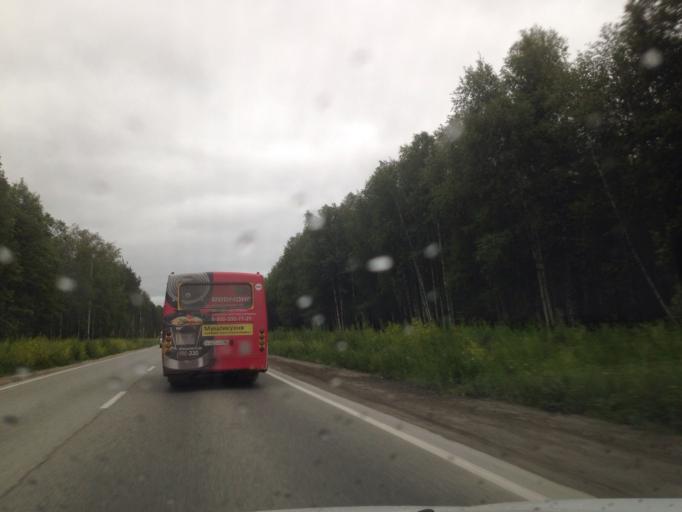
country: RU
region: Sverdlovsk
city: Istok
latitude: 56.8434
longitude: 60.7321
